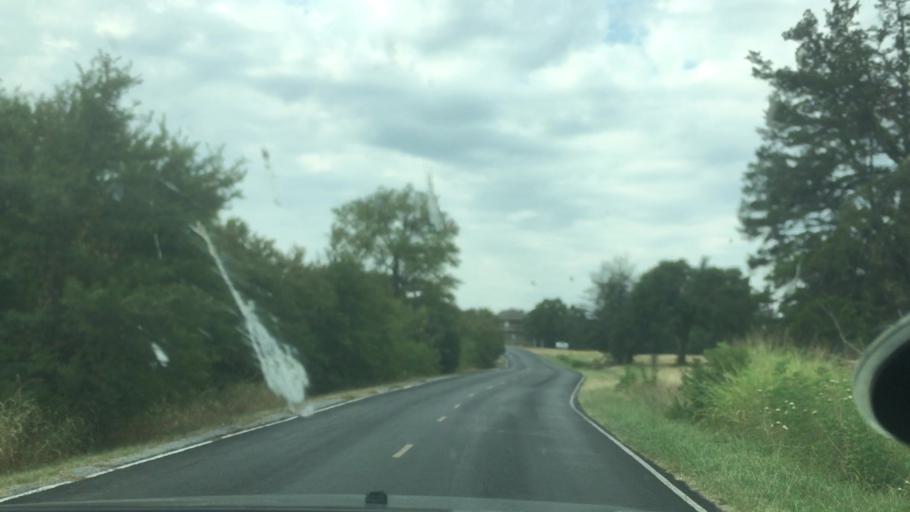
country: US
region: Texas
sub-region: Grayson County
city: Pottsboro
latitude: 33.8183
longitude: -96.7077
